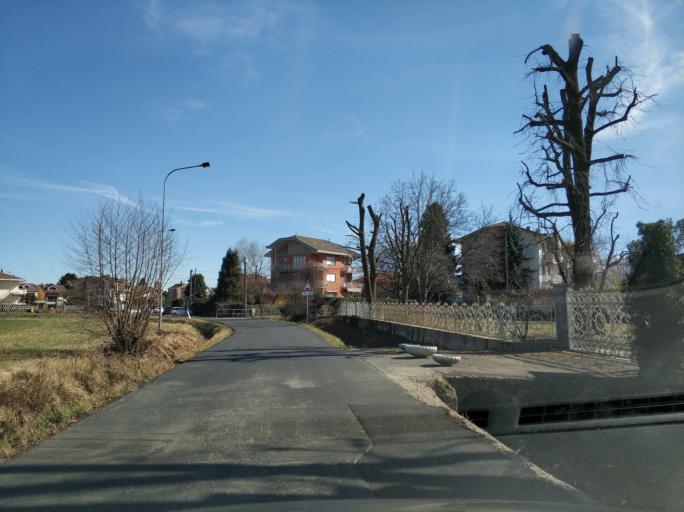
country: IT
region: Piedmont
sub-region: Provincia di Torino
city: Leini
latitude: 45.1869
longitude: 7.7066
